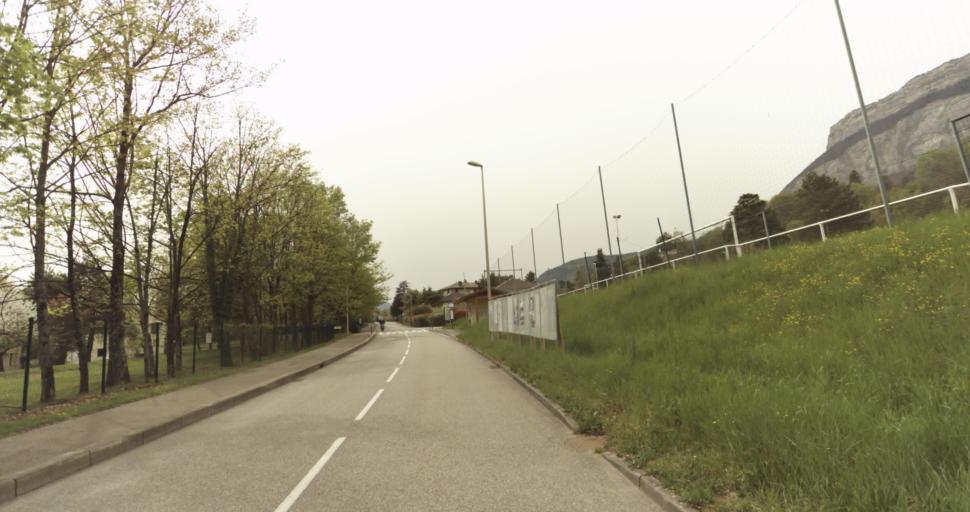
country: FR
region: Rhone-Alpes
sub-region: Departement de l'Isere
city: Montbonnot-Saint-Martin
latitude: 45.2224
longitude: 5.8005
